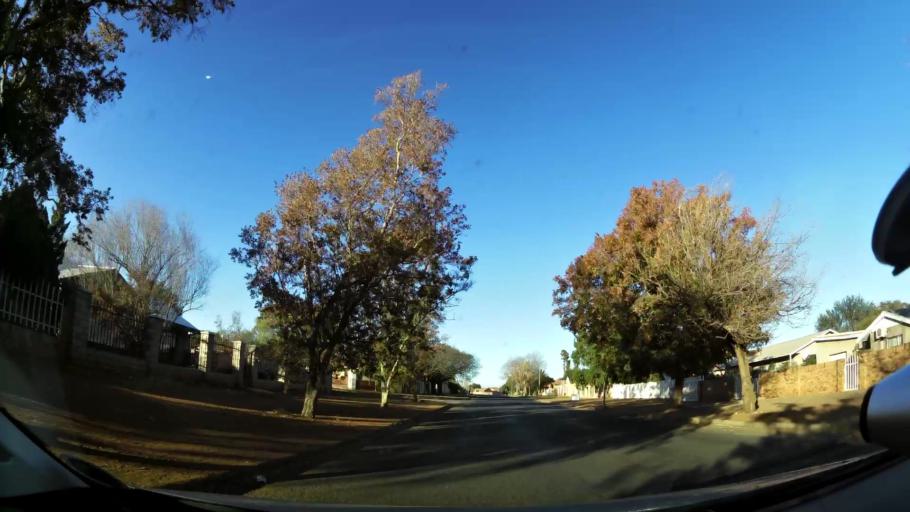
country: ZA
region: Northern Cape
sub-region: Frances Baard District Municipality
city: Kimberley
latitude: -28.7546
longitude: 24.7405
